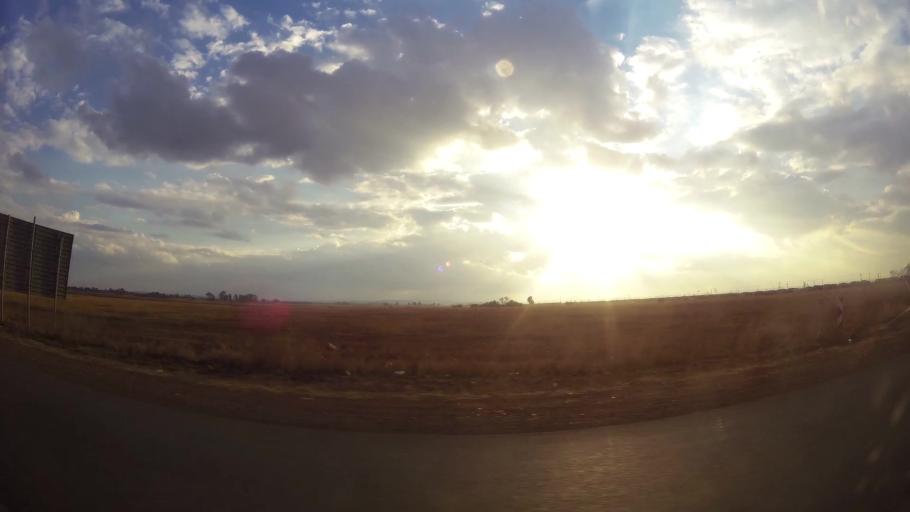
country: ZA
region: Gauteng
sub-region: Sedibeng District Municipality
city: Vanderbijlpark
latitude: -26.6216
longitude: 27.8118
